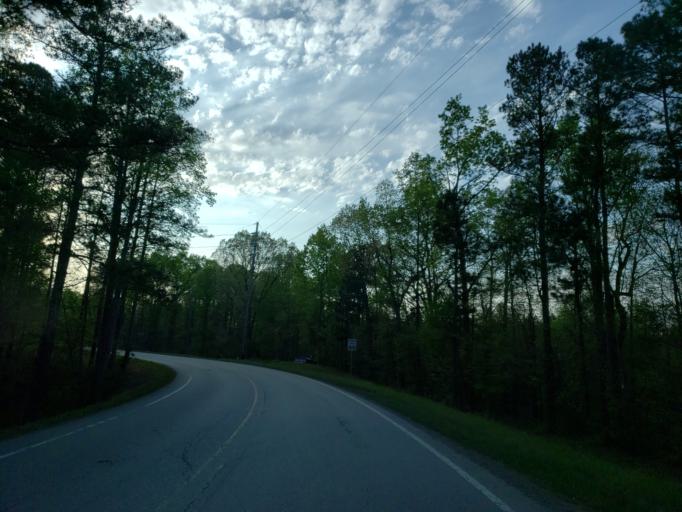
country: US
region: Georgia
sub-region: Cherokee County
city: Ball Ground
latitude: 34.2919
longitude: -84.3863
